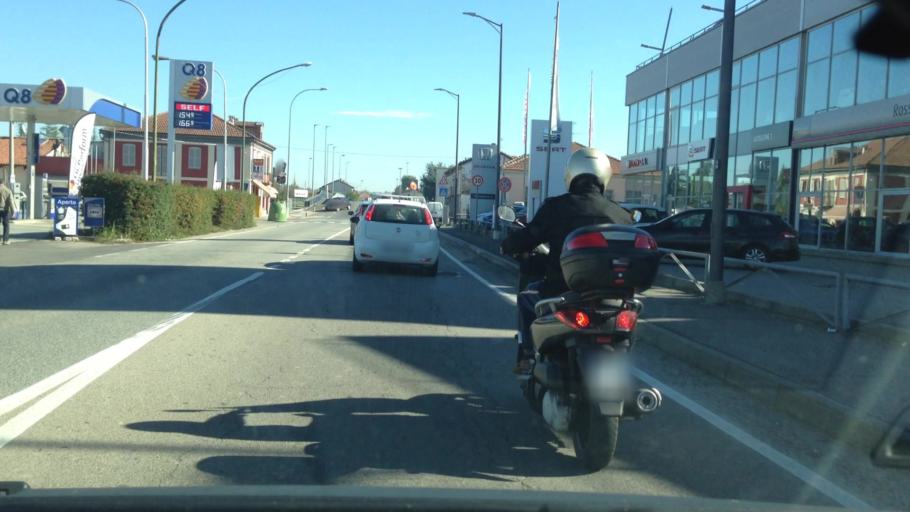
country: IT
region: Piedmont
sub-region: Provincia di Asti
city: Asti
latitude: 44.9058
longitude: 8.2353
